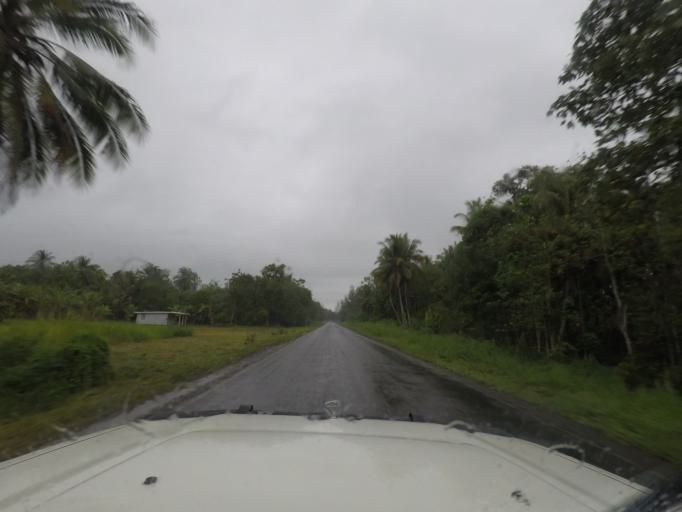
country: PG
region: Madang
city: Madang
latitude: -5.3560
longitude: 145.7102
